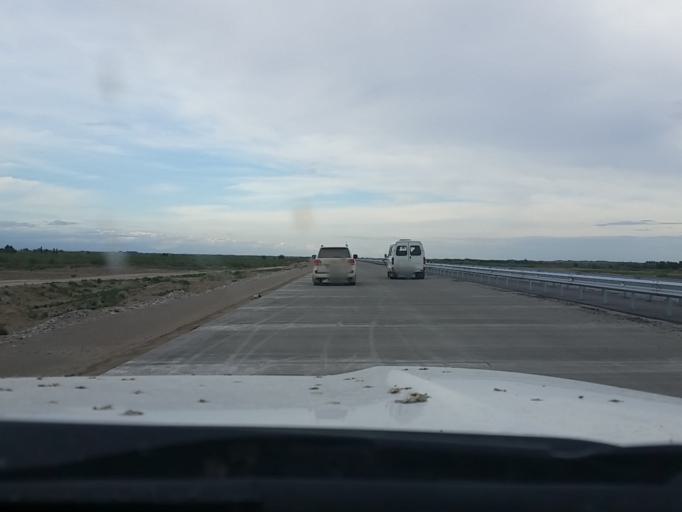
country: KZ
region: Almaty Oblysy
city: Zharkent
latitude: 44.1010
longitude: 80.0714
